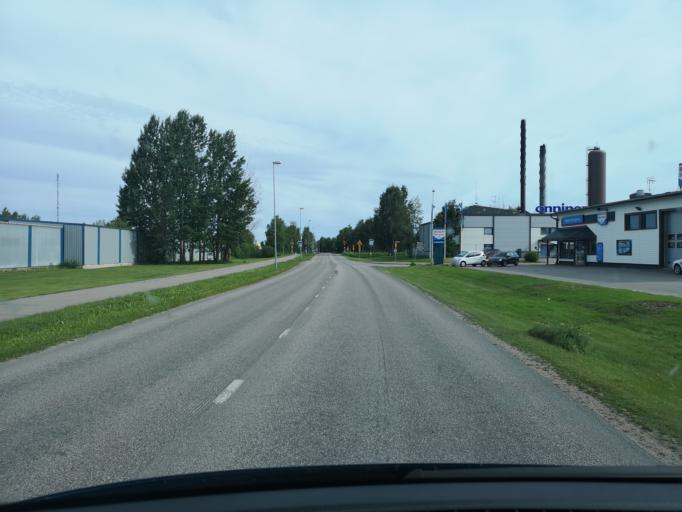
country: FI
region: Northern Ostrobothnia
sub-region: Ylivieska
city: Ylivieska
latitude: 64.0673
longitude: 24.5507
